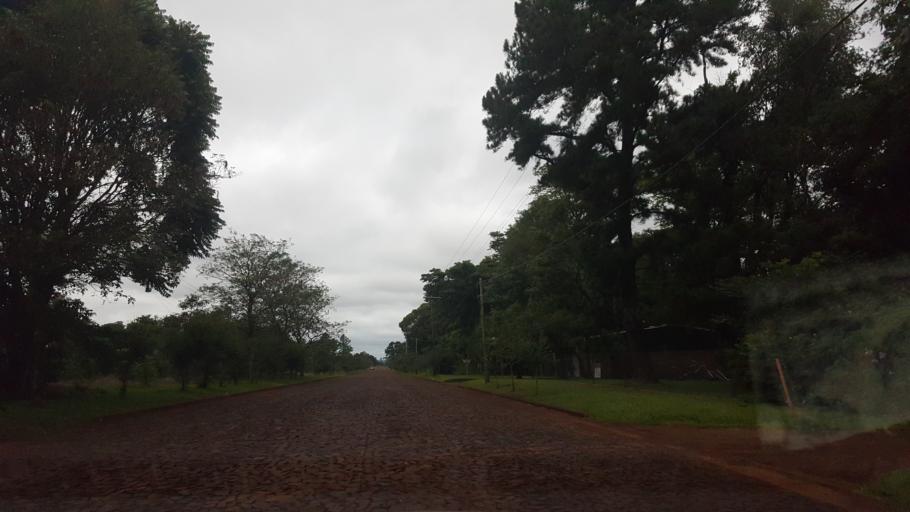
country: AR
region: Misiones
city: Capiovi
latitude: -26.9541
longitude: -55.0557
